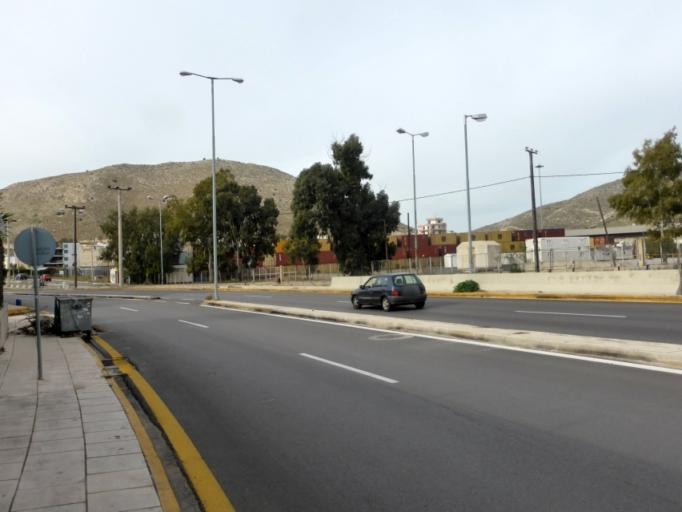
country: GR
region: Attica
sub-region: Nomos Piraios
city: Keratsini
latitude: 37.9619
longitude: 23.6108
